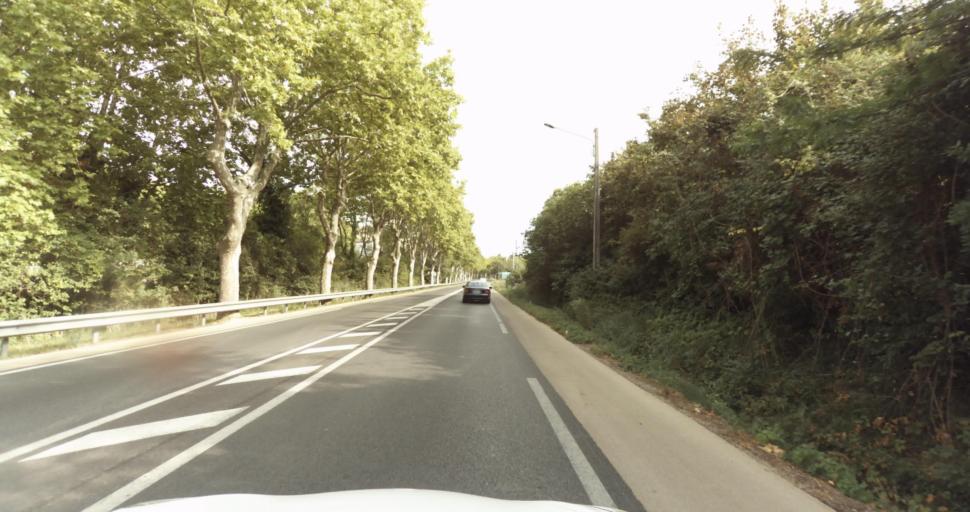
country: FR
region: Provence-Alpes-Cote d'Azur
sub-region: Departement des Bouches-du-Rhone
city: Saint-Chamas
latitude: 43.5695
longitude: 5.0221
